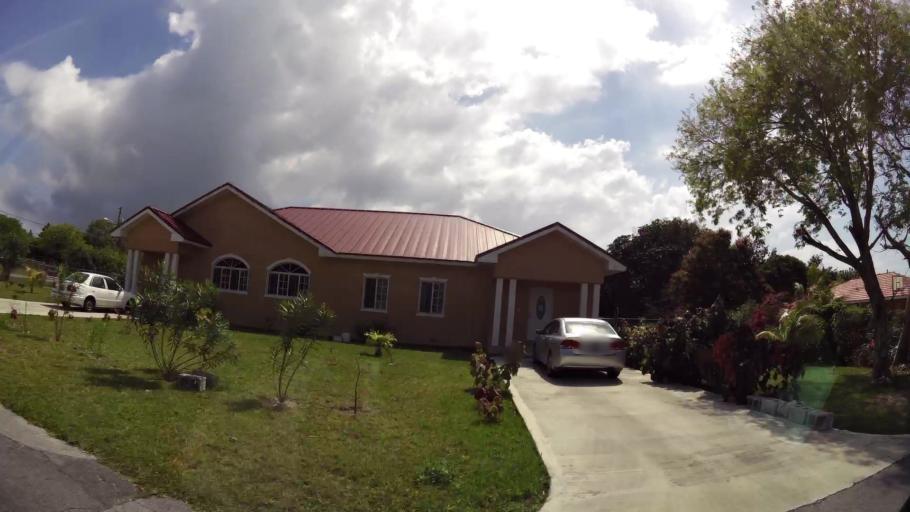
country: BS
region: Freeport
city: Freeport
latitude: 26.5038
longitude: -78.7056
